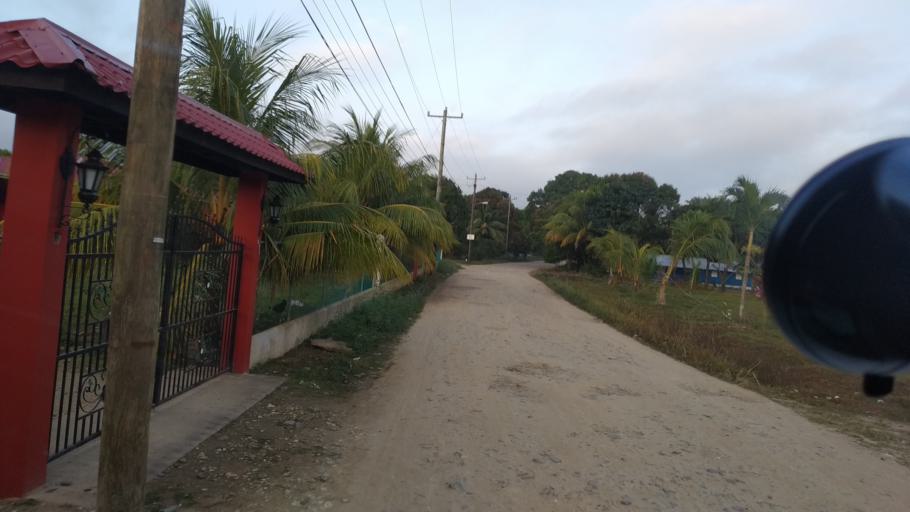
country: BZ
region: Stann Creek
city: Placencia
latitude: 16.5710
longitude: -88.5261
